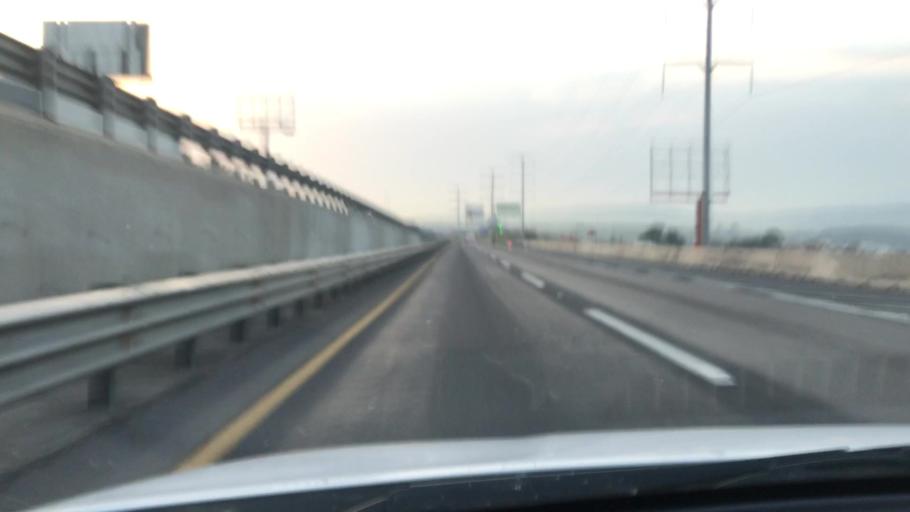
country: MX
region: Jalisco
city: Tonala
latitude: 20.6163
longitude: -103.2452
